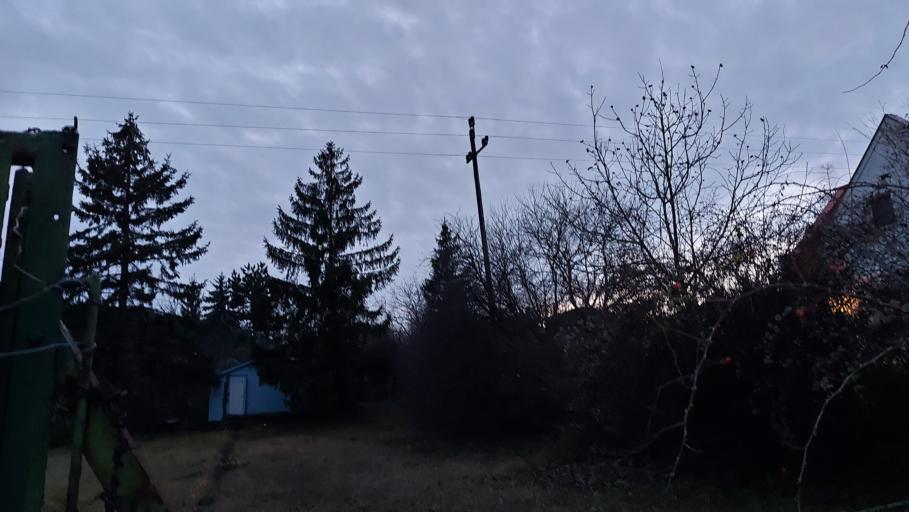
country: HU
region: Pest
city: Budaors
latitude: 47.4708
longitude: 18.9531
